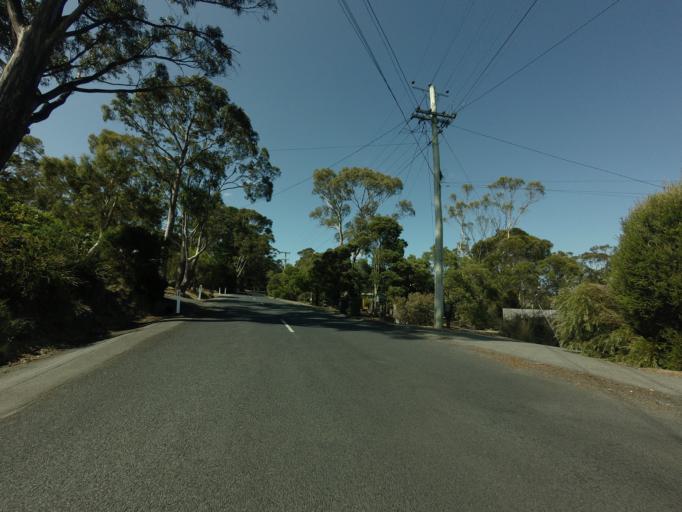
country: AU
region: Tasmania
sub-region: Kingborough
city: Taroona
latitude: -42.9261
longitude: 147.3390
